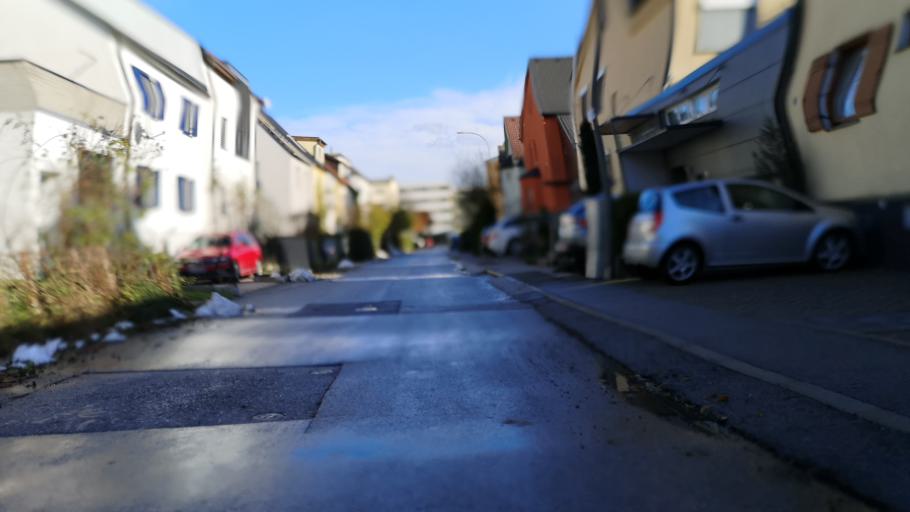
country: AT
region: Tyrol
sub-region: Innsbruck Stadt
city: Innsbruck
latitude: 47.2638
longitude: 11.3685
